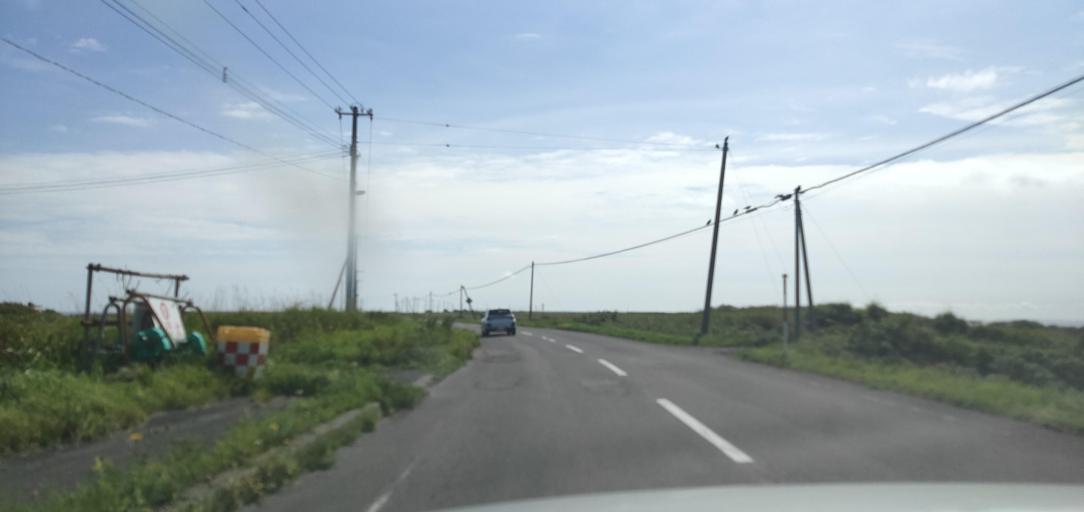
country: JP
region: Hokkaido
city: Shibetsu
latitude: 43.6283
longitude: 145.1957
